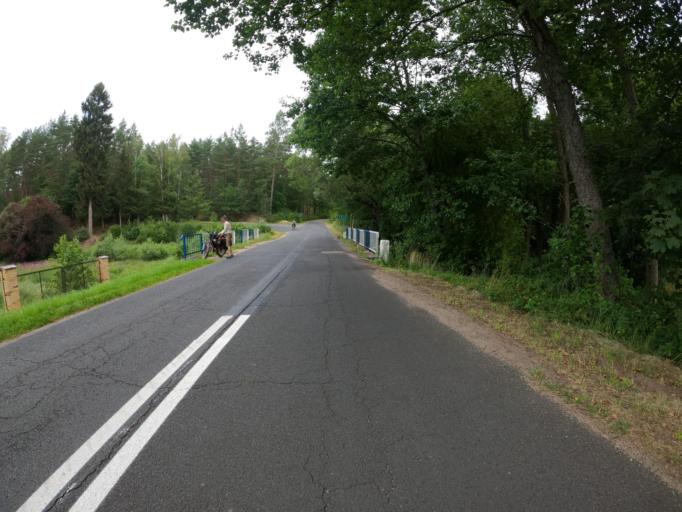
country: PL
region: West Pomeranian Voivodeship
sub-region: Powiat szczecinecki
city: Grzmiaca
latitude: 53.7801
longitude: 16.4985
